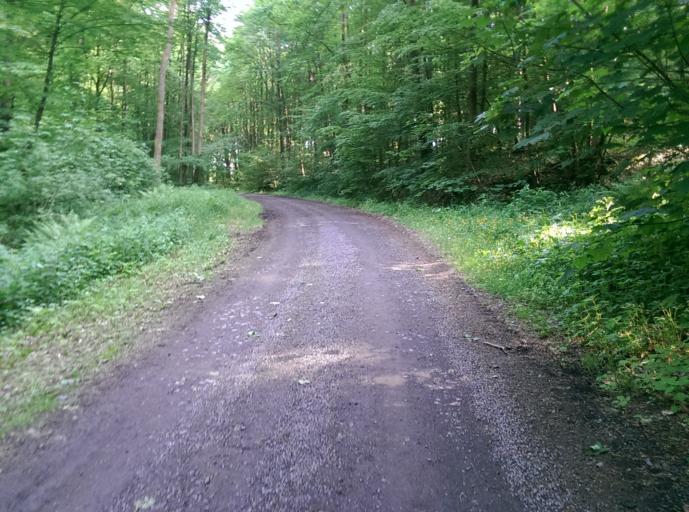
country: DE
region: Rheinland-Pfalz
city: Ehlscheid
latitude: 50.4846
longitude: 7.4449
